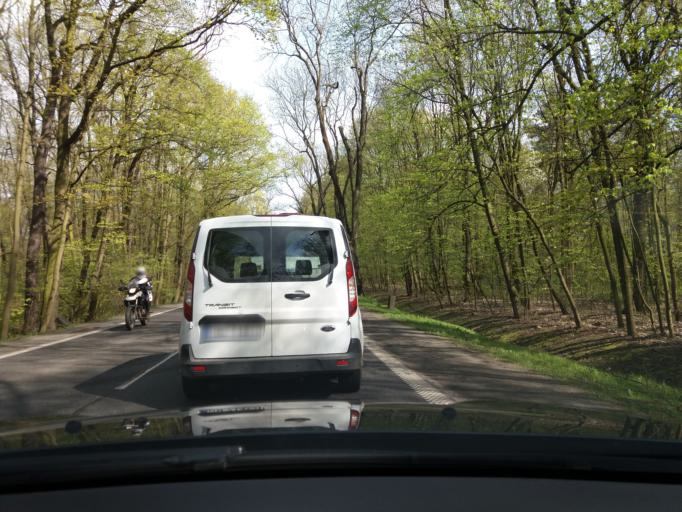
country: PL
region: Lower Silesian Voivodeship
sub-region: Powiat sredzki
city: Mrozow
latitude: 51.1483
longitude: 16.8460
